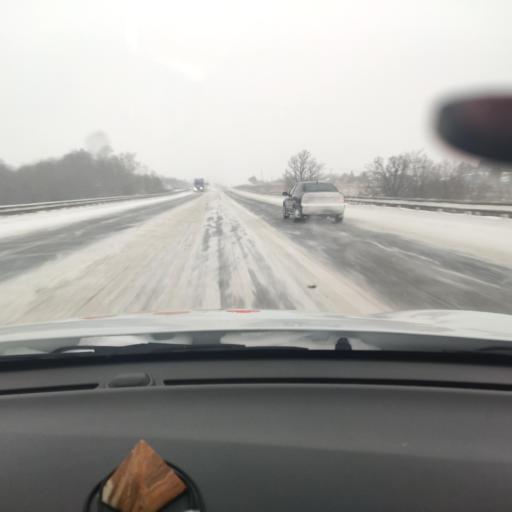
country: RU
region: Tatarstan
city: Verkhniy Uslon
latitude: 55.7209
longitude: 48.8349
